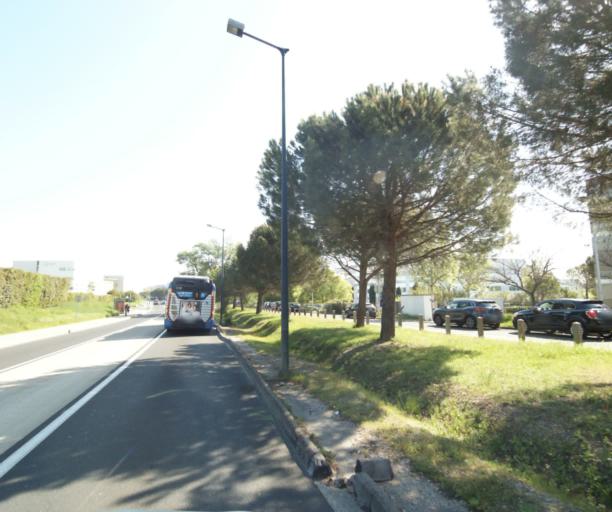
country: FR
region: Languedoc-Roussillon
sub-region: Departement de l'Herault
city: Castelnau-le-Lez
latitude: 43.6153
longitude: 3.9090
